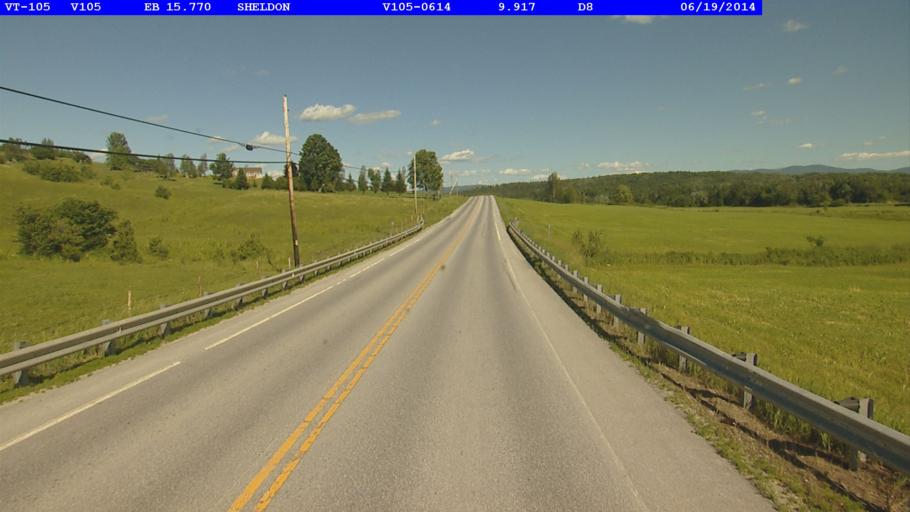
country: US
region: Vermont
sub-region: Franklin County
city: Enosburg Falls
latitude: 44.9084
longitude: -72.8417
